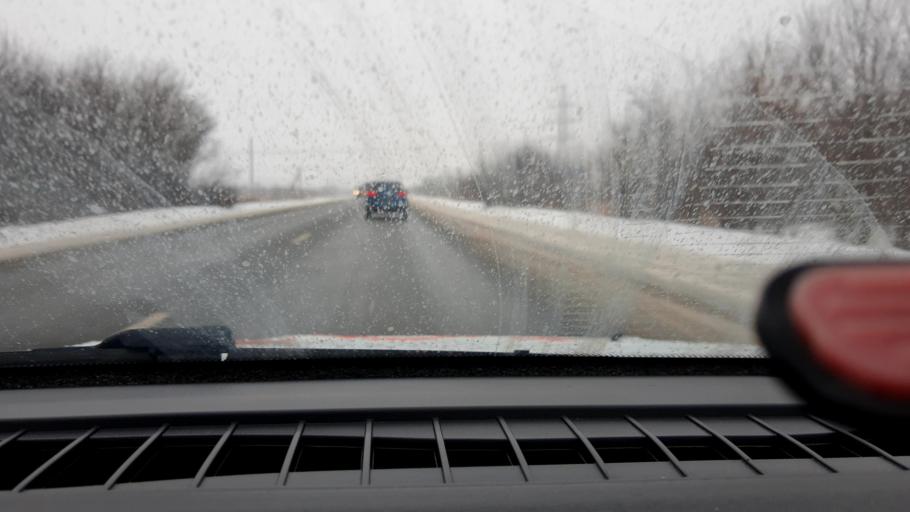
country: RU
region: Nizjnij Novgorod
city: Kstovo
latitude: 56.1143
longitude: 44.1823
